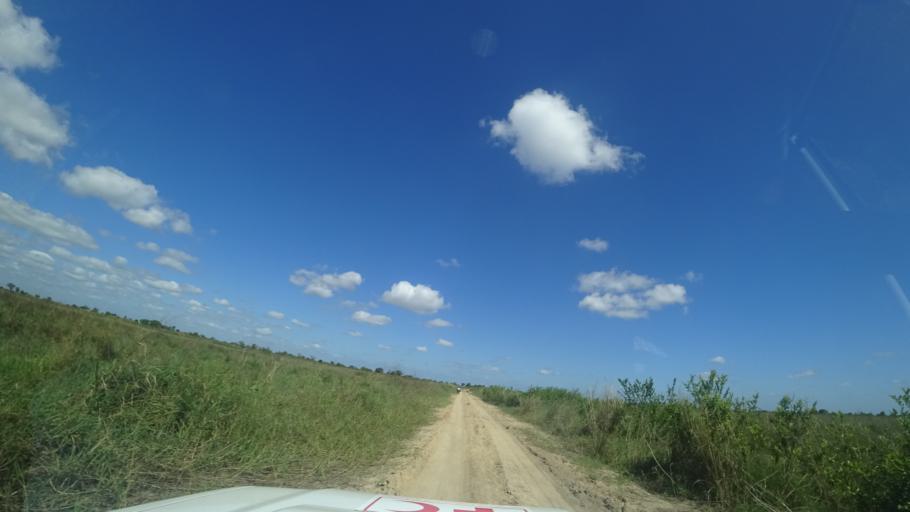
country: MZ
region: Sofala
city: Dondo
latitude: -19.3976
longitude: 34.5708
